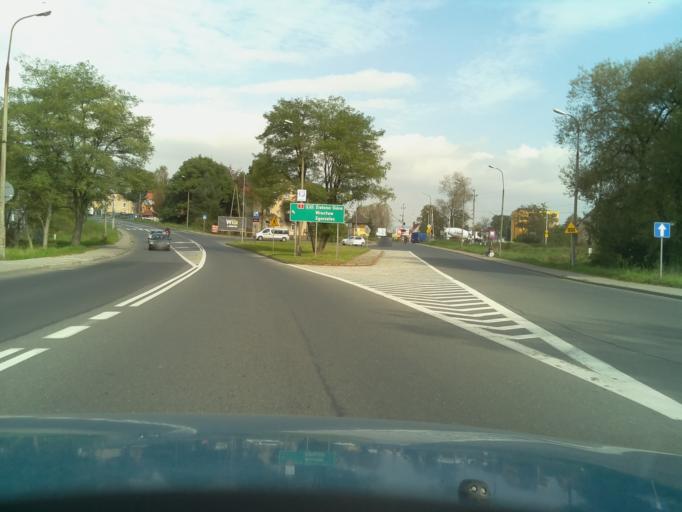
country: PL
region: Lower Silesian Voivodeship
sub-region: Jelenia Gora
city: Jelenia Gora
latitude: 50.8957
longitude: 15.7150
